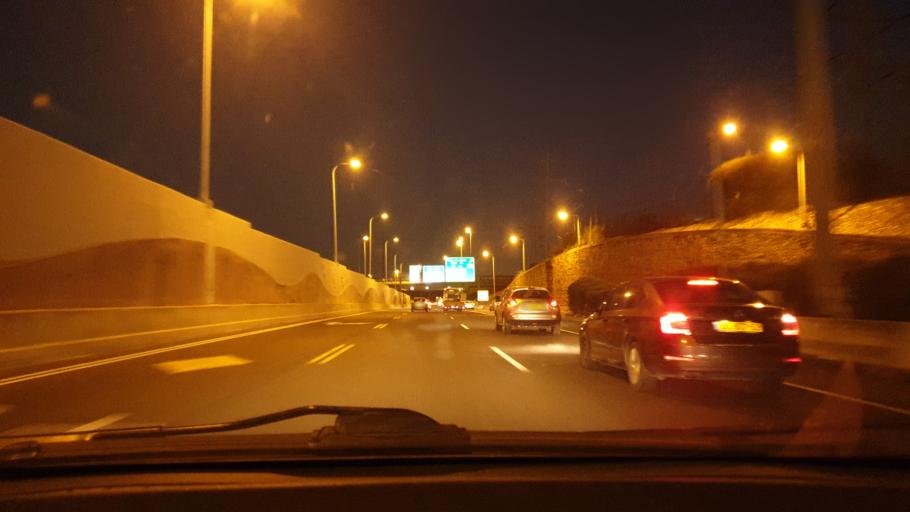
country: IL
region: Tel Aviv
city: Yafo
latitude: 32.0372
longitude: 34.7670
